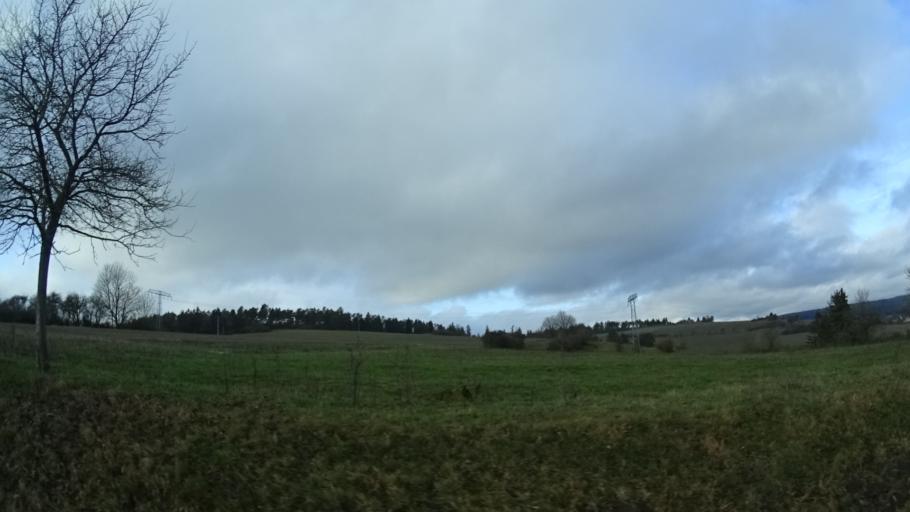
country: DE
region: Thuringia
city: Utendorf
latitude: 50.5984
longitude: 10.4387
